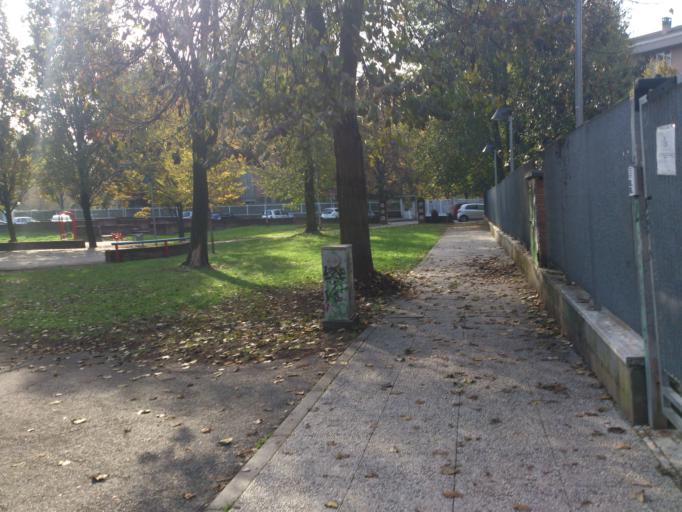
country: IT
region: Lombardy
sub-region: Citta metropolitana di Milano
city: San Donato Milanese
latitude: 45.4289
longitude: 9.2673
